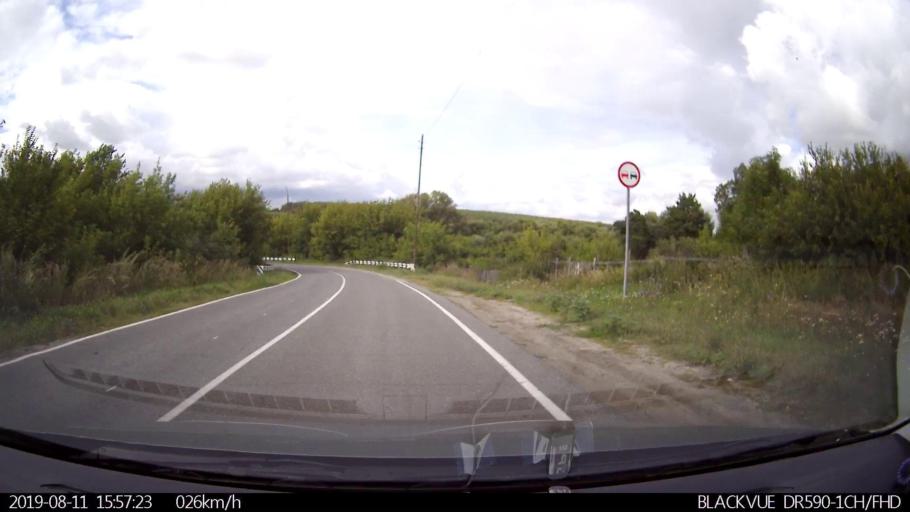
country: RU
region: Ulyanovsk
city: Ignatovka
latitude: 53.9508
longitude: 47.6525
